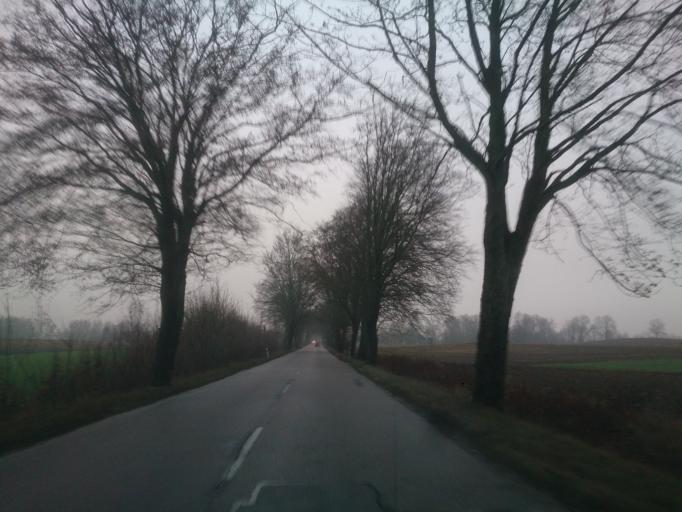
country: PL
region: Pomeranian Voivodeship
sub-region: Powiat koscierski
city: Stara Kiszewa
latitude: 54.0307
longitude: 18.0954
